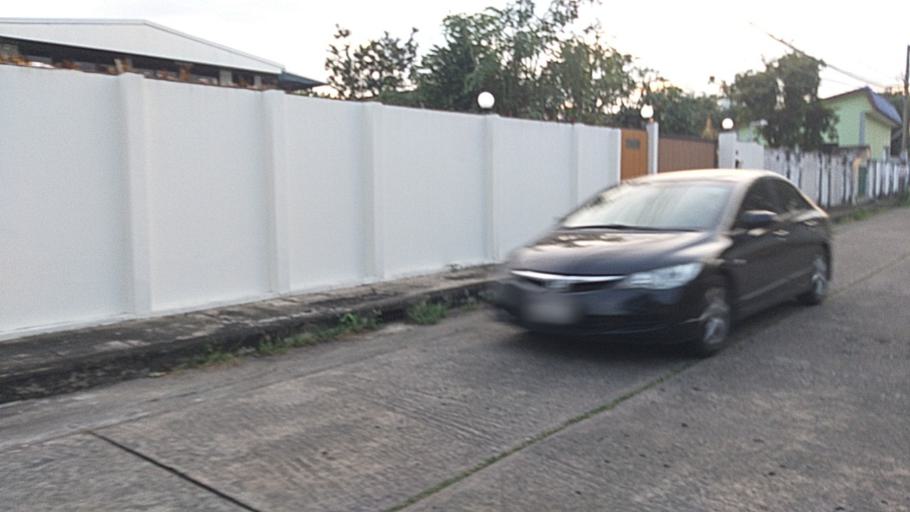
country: TH
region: Bangkok
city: Lat Phrao
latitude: 13.8299
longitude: 100.6094
